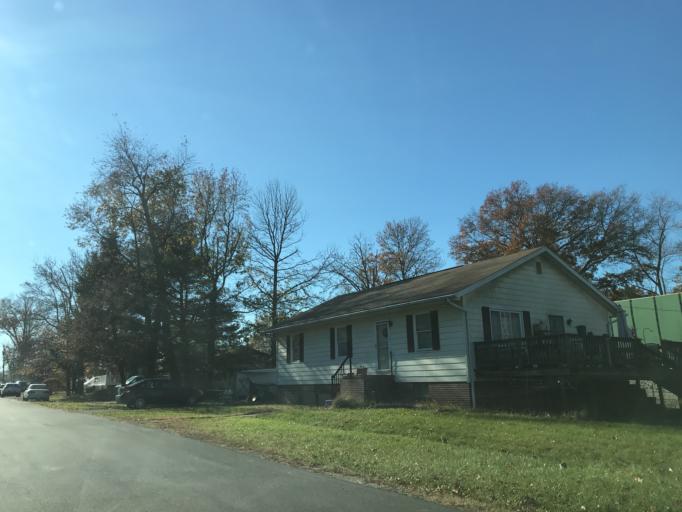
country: US
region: Maryland
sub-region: Baltimore County
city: Bowleys Quarters
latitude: 39.3748
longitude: -76.3514
